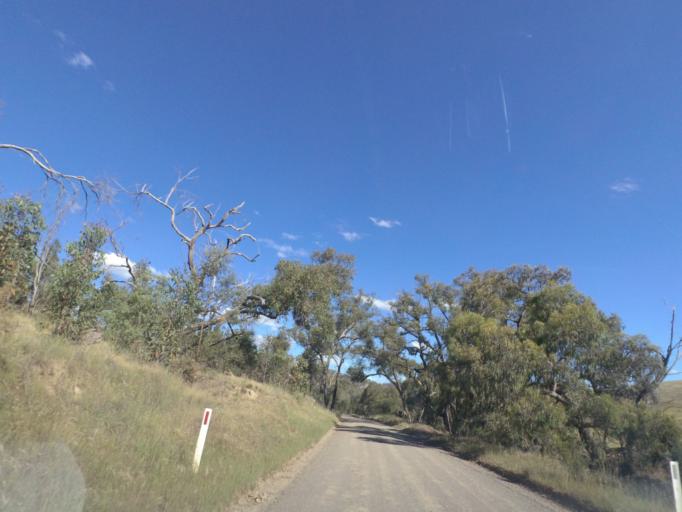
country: AU
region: Victoria
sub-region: Hume
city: Craigieburn
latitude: -37.4217
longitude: 144.9224
